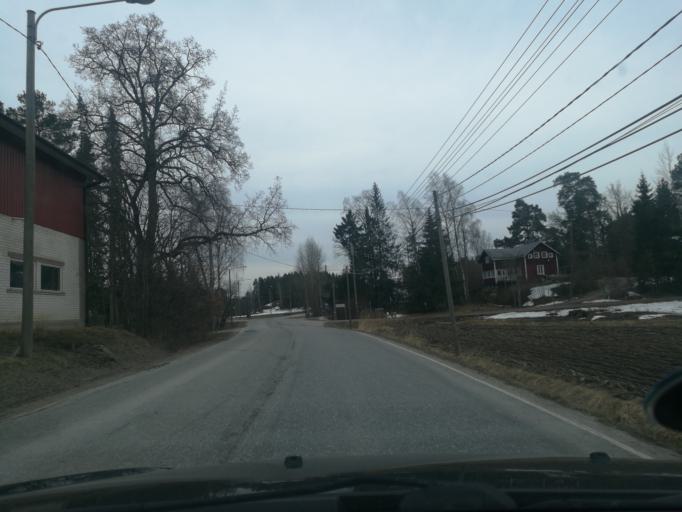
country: FI
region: Uusimaa
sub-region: Helsinki
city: Nickby
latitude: 60.2879
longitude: 25.3670
